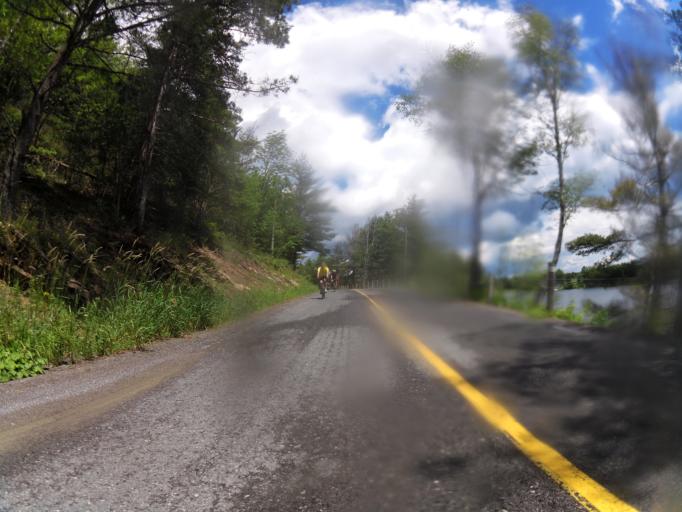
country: CA
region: Ontario
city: Renfrew
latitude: 45.0633
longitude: -76.6546
